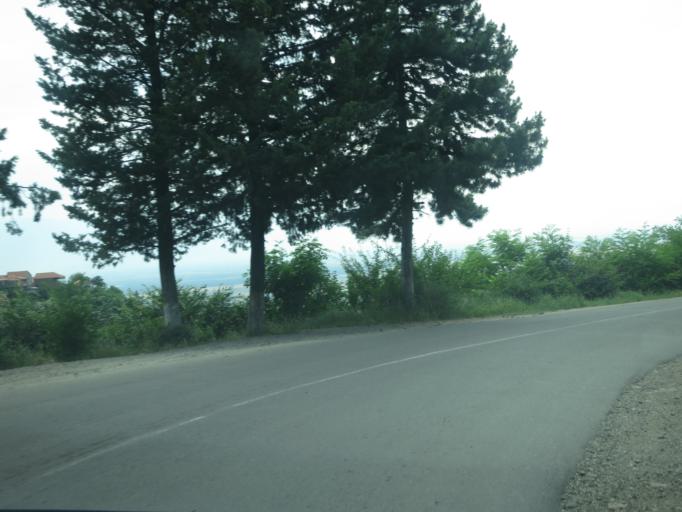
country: GE
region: Kakheti
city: Sighnaghi
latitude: 41.6143
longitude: 45.9212
